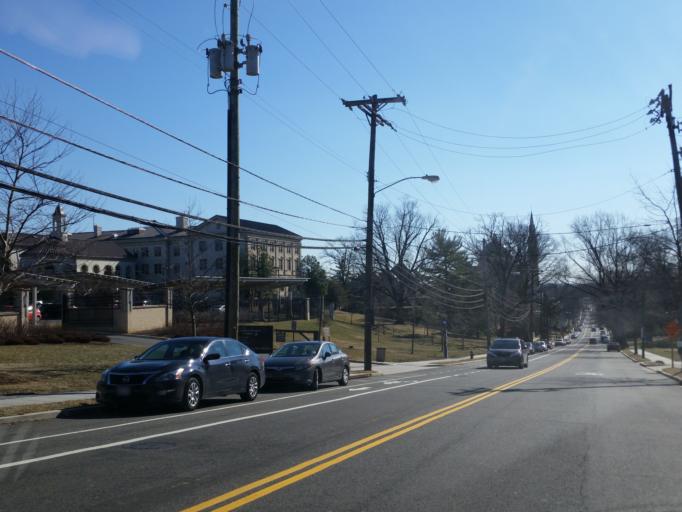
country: US
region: Maryland
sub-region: Prince George's County
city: Chillum
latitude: 38.9395
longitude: -77.0028
